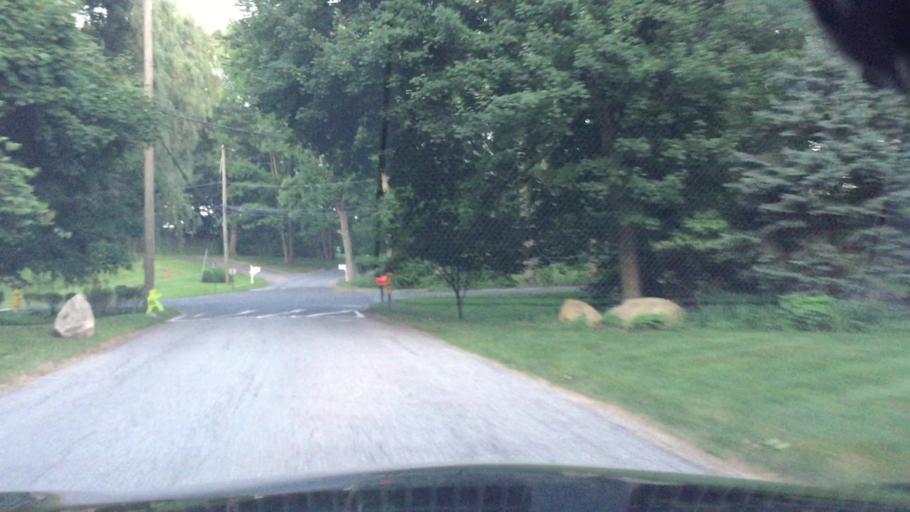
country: US
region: Connecticut
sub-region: Fairfield County
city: Darien
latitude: 41.0702
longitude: -73.4277
